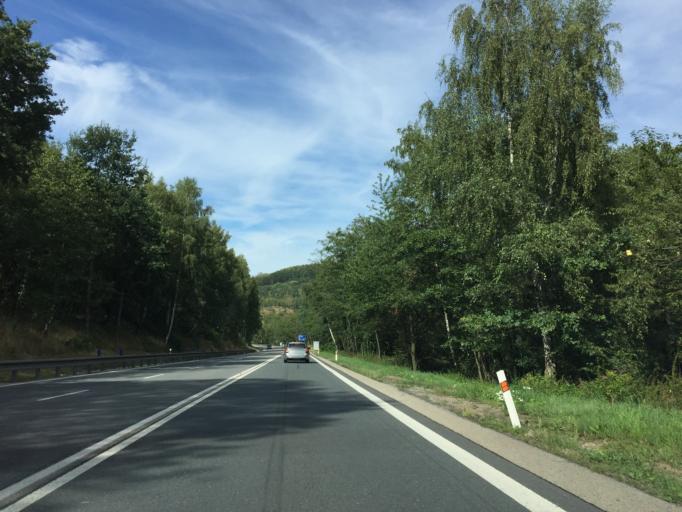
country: CZ
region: Central Bohemia
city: Votice
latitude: 49.6328
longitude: 14.6511
